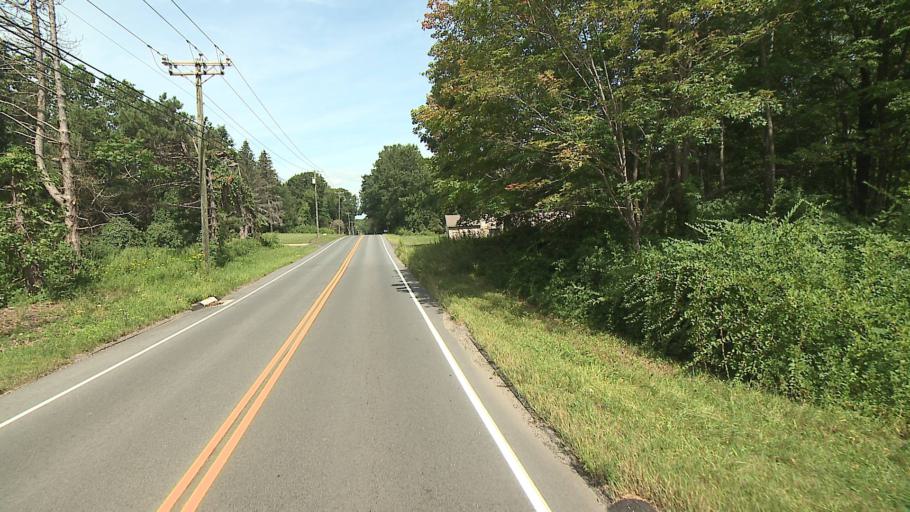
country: US
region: Connecticut
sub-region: Litchfield County
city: Bethlehem Village
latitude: 41.6212
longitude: -73.1997
